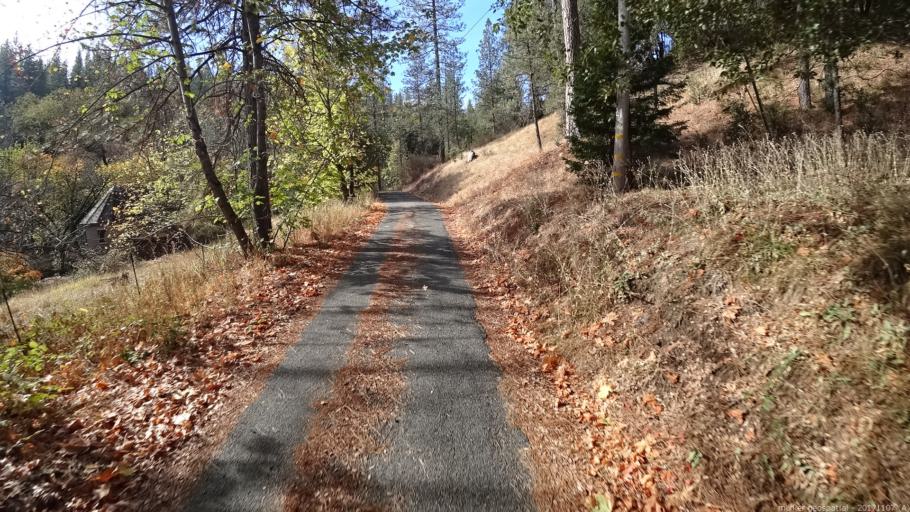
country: US
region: California
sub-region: Shasta County
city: Shasta
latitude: 40.5423
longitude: -122.5813
